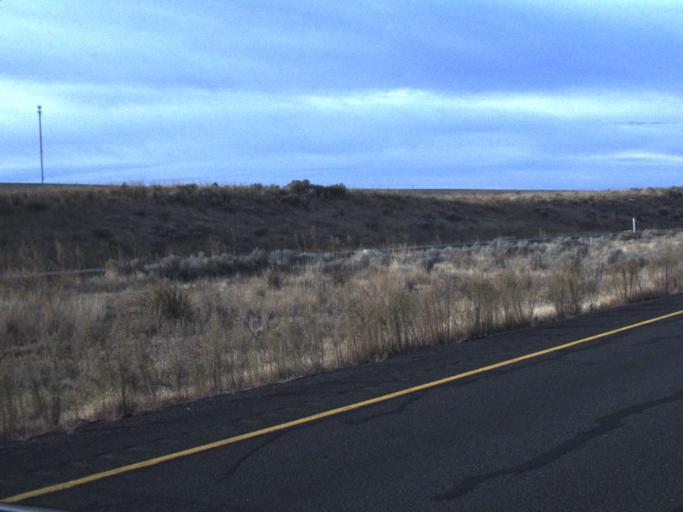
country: US
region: Washington
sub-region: Franklin County
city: Connell
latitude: 46.8311
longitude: -118.6602
